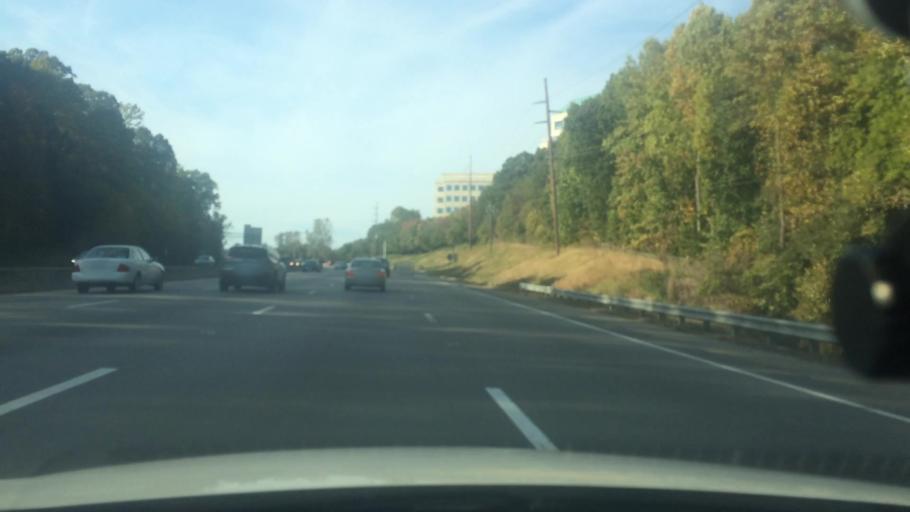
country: US
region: North Carolina
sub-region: Wake County
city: Raleigh
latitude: 35.8183
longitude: -78.6079
